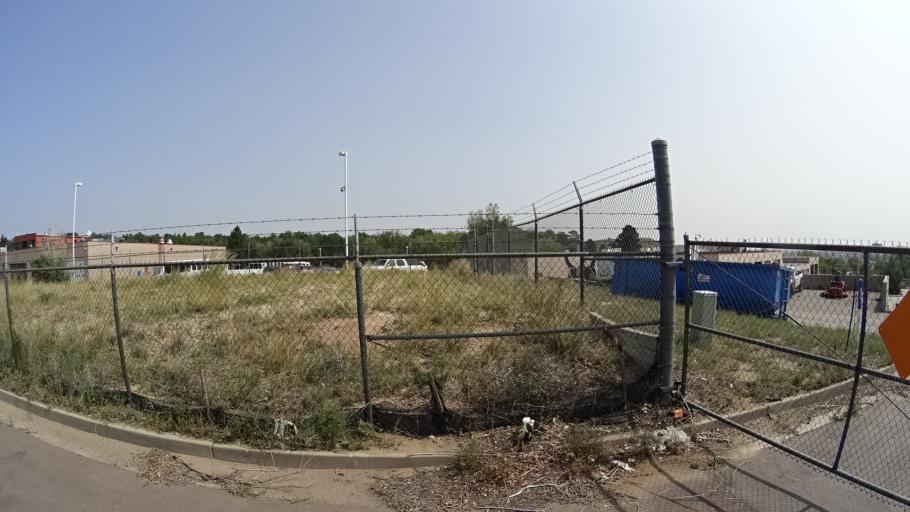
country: US
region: Colorado
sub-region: El Paso County
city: Colorado Springs
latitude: 38.8154
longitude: -104.8060
